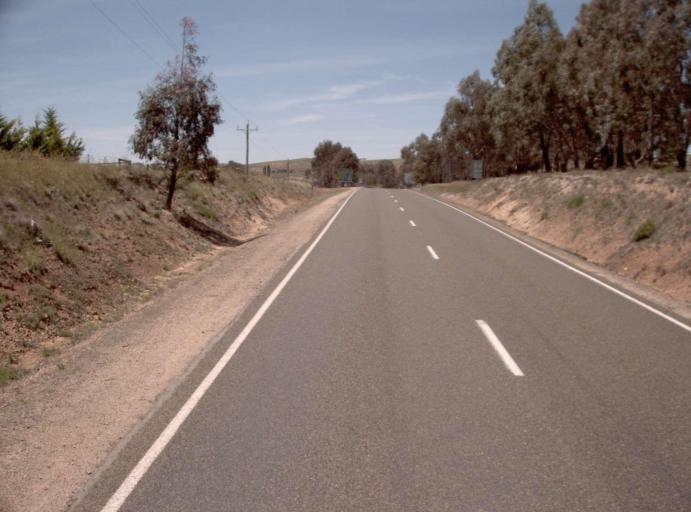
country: AU
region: Victoria
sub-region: Alpine
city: Mount Beauty
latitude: -37.1012
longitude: 147.6013
